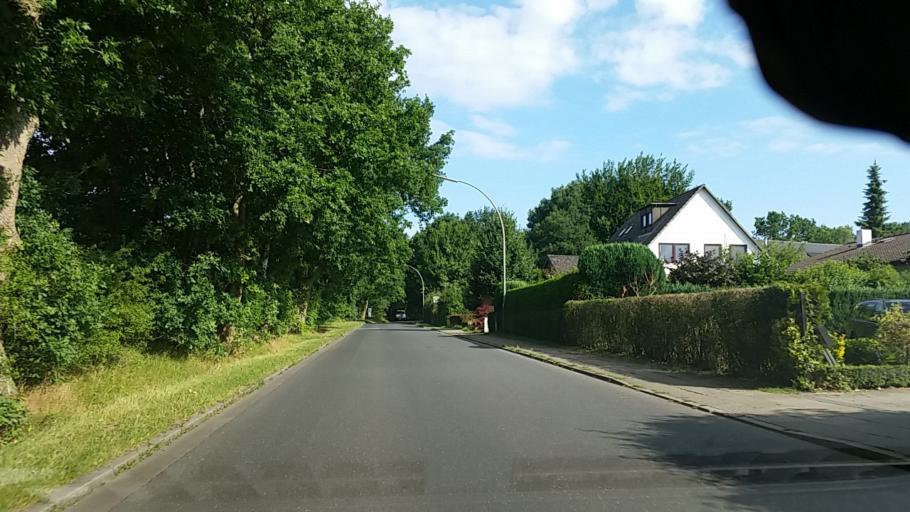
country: DE
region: Hamburg
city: Hummelsbuettel
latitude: 53.6716
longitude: 10.0559
